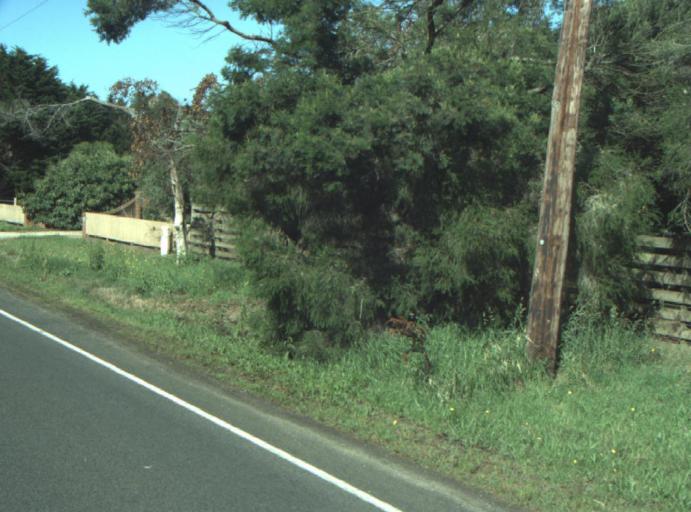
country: AU
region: Victoria
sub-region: Greater Geelong
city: Clifton Springs
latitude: -38.2583
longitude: 144.5589
